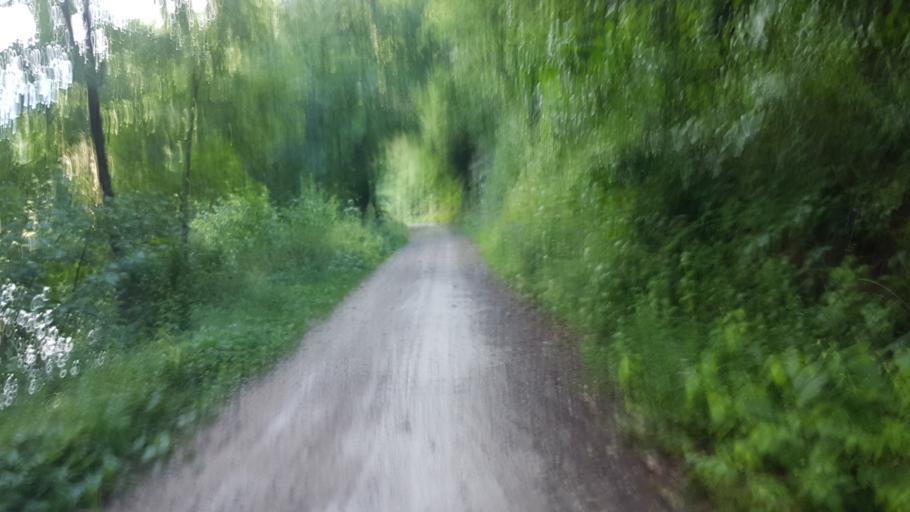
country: DE
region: Baden-Wuerttemberg
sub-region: Tuebingen Region
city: Stetten am Kalten Markt
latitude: 48.0855
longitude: 9.0644
